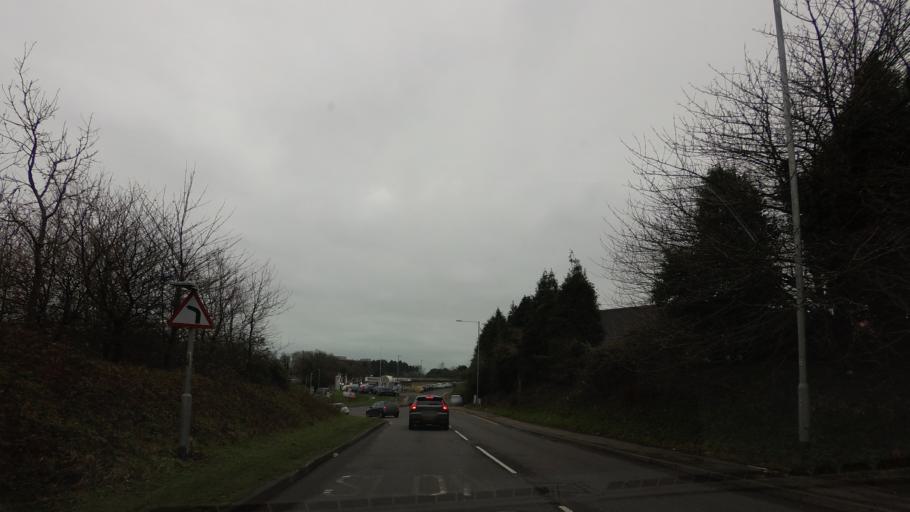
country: GB
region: England
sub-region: East Sussex
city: Saint Leonards-on-Sea
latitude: 50.8903
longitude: 0.5543
